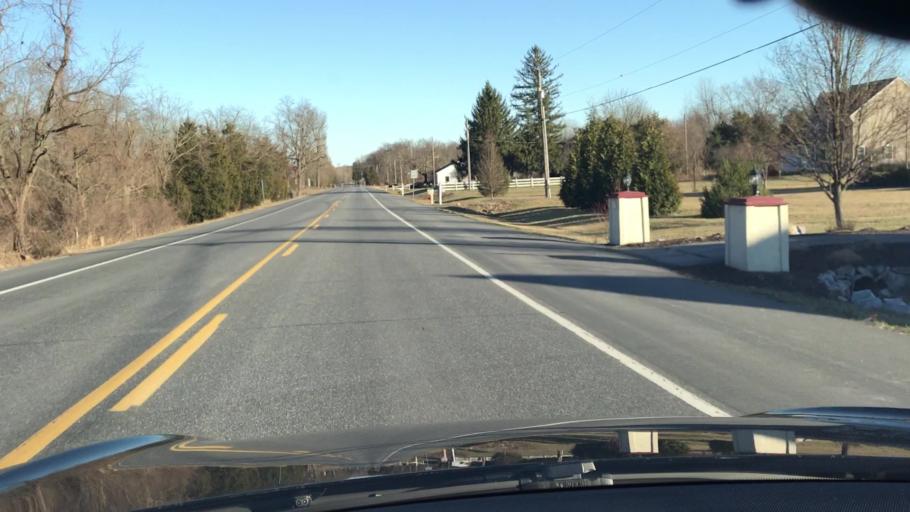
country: US
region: Pennsylvania
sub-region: York County
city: Valley Green
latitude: 40.1442
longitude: -76.8752
